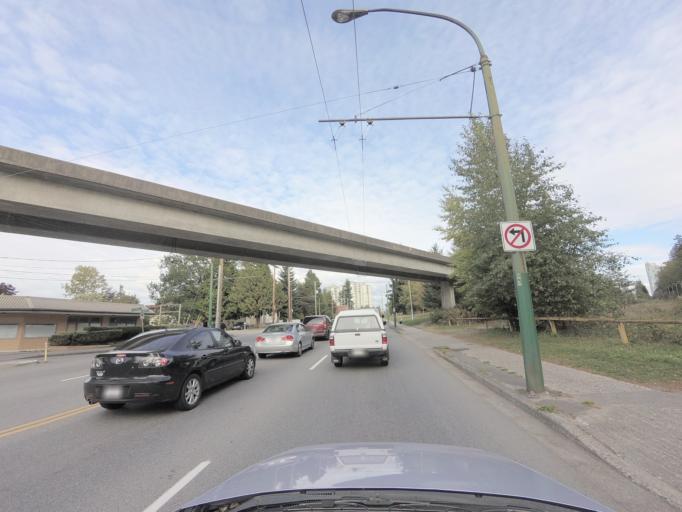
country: CA
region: British Columbia
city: Burnaby
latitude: 49.2326
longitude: -123.0192
